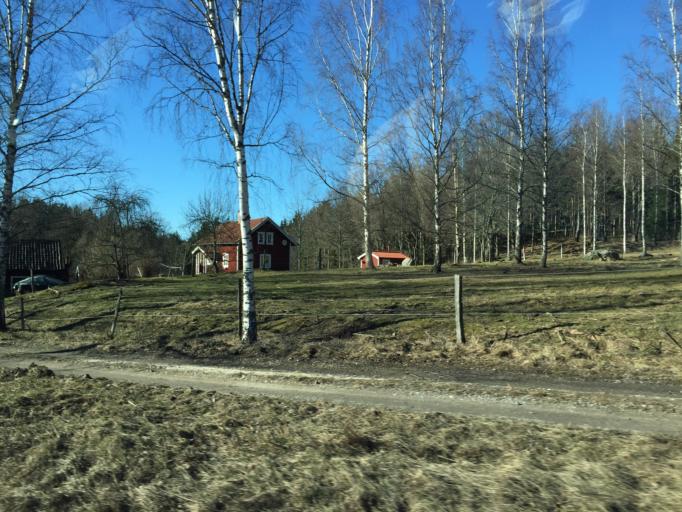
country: SE
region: OEstergoetland
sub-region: Finspangs Kommun
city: Finspang
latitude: 58.7088
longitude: 15.7349
